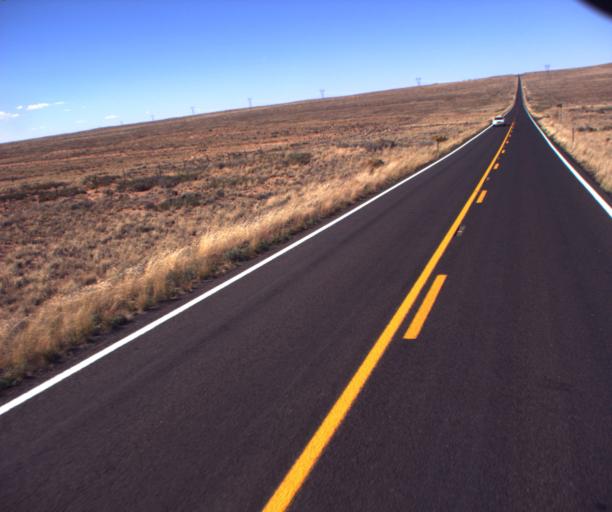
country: US
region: Arizona
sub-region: Coconino County
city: Tuba City
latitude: 35.9423
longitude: -110.9096
